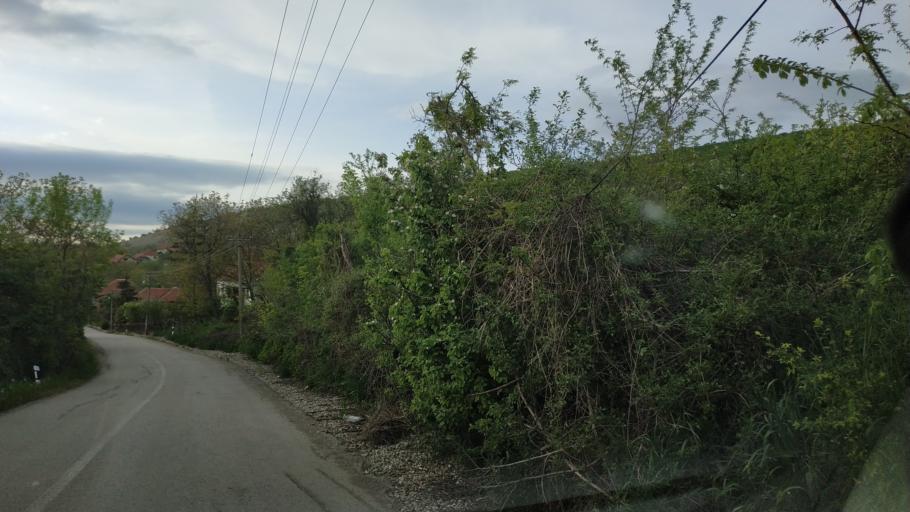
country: RS
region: Central Serbia
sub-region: Zajecarski Okrug
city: Soko Banja
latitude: 43.5265
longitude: 21.8570
